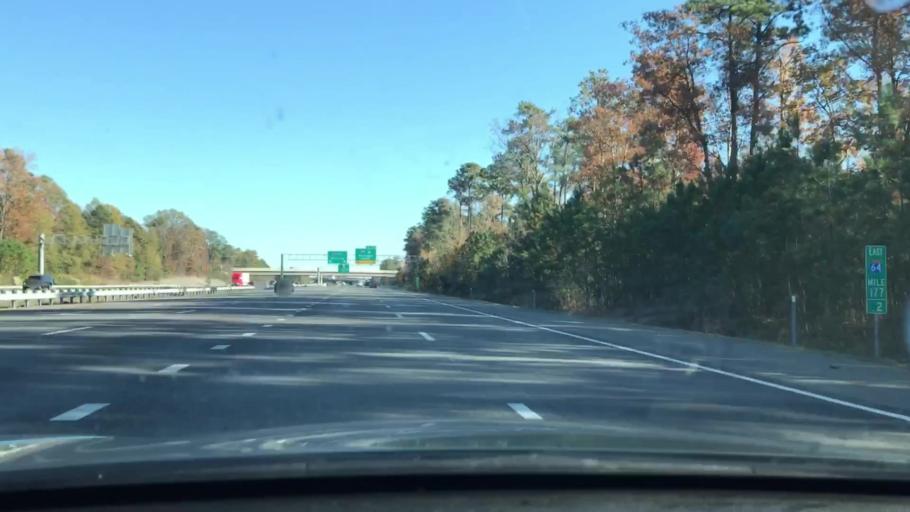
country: US
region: Virginia
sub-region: Henrico County
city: Short Pump
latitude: 37.6587
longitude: -77.6169
